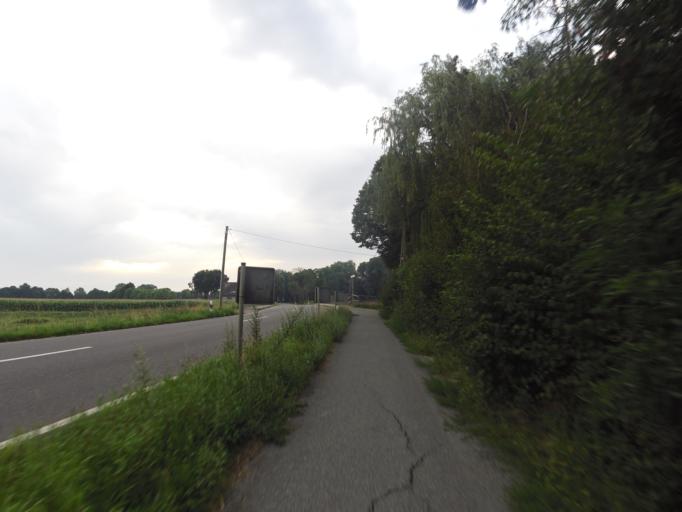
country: NL
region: Gelderland
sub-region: Oude IJsselstreek
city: Gendringen
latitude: 51.8650
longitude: 6.3905
